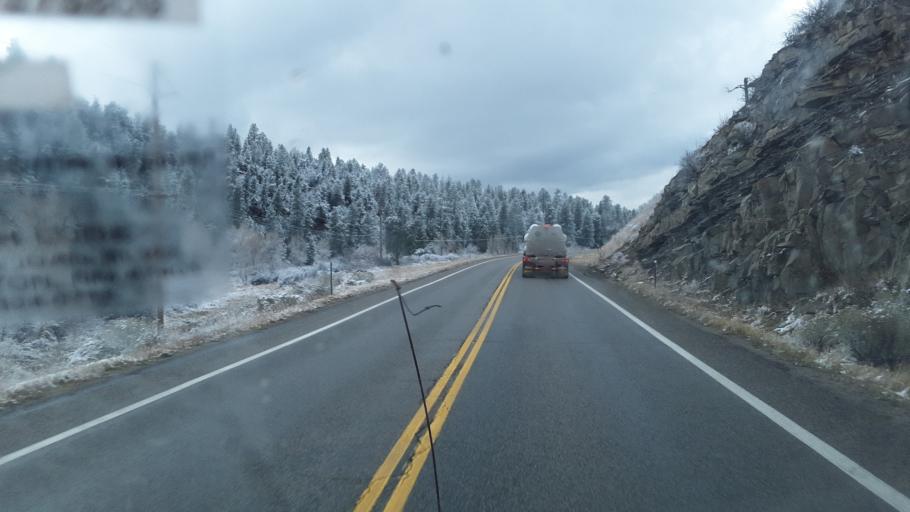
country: US
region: Colorado
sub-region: Archuleta County
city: Pagosa Springs
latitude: 37.2085
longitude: -107.2419
